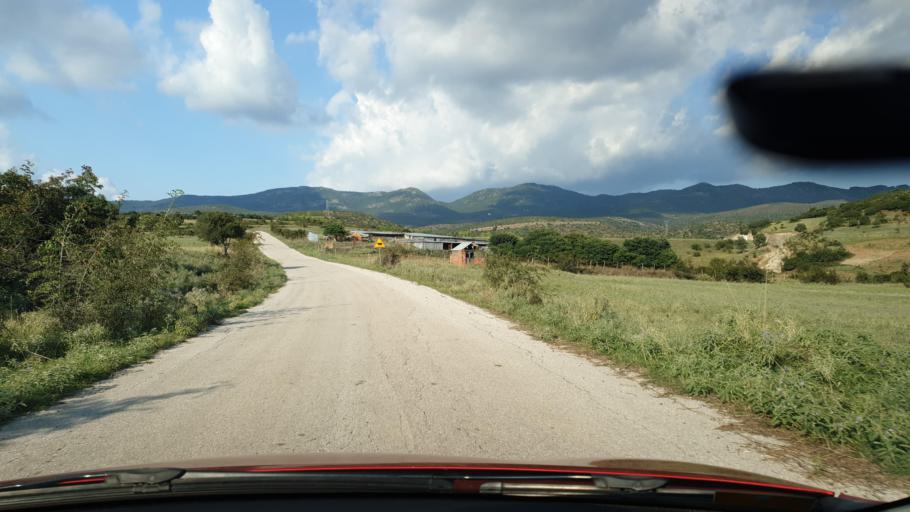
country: GR
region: Central Macedonia
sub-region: Nomos Thessalonikis
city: Vasilika
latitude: 40.5034
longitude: 23.1484
